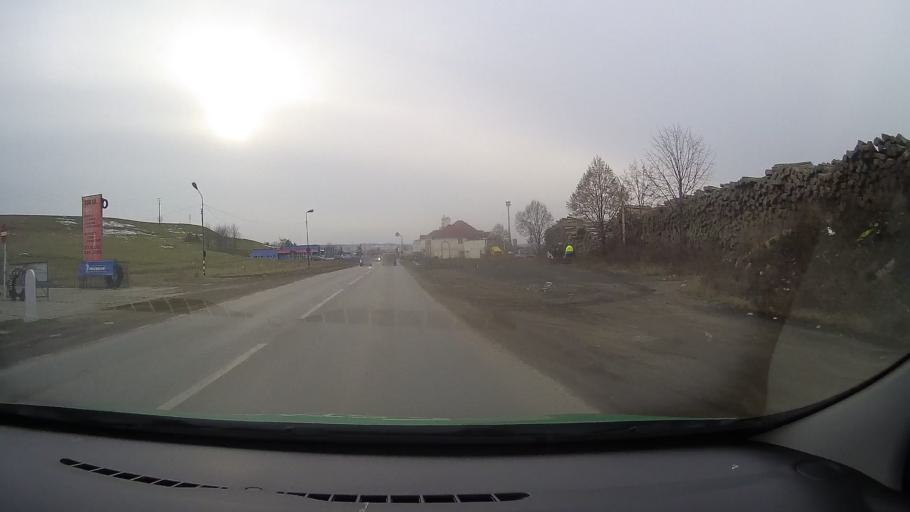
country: RO
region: Hunedoara
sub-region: Municipiul Orastie
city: Orastie
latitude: 45.8630
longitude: 23.2187
